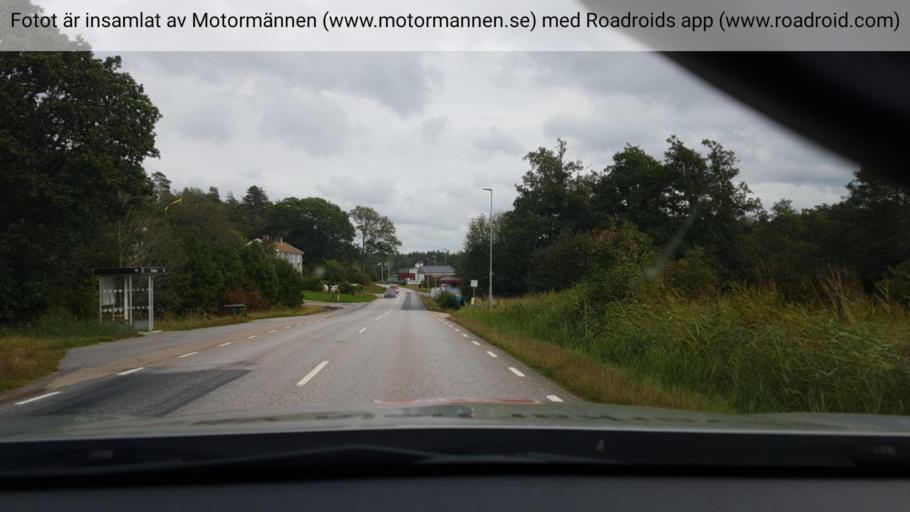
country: SE
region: Vaestra Goetaland
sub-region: Sotenas Kommun
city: Hunnebostrand
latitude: 58.5660
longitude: 11.3771
